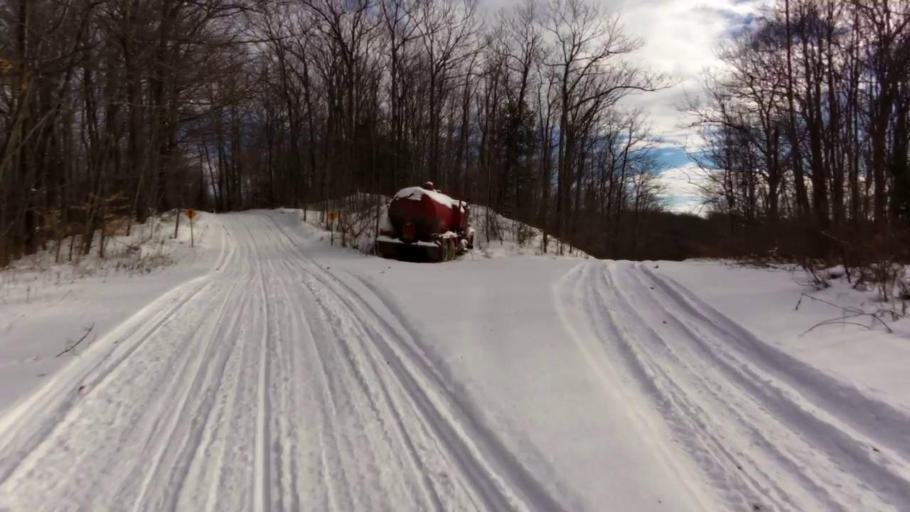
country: US
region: Pennsylvania
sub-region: McKean County
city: Foster Brook
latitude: 42.0038
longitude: -78.5814
